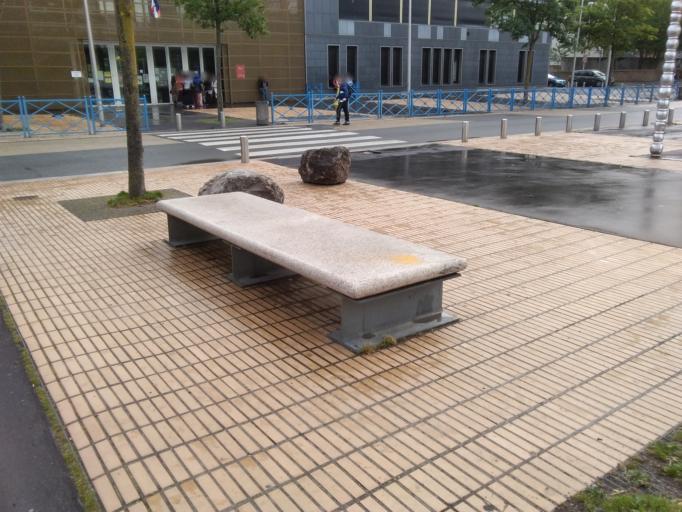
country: FR
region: Picardie
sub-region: Departement de la Somme
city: Amiens
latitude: 49.9115
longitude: 2.3002
